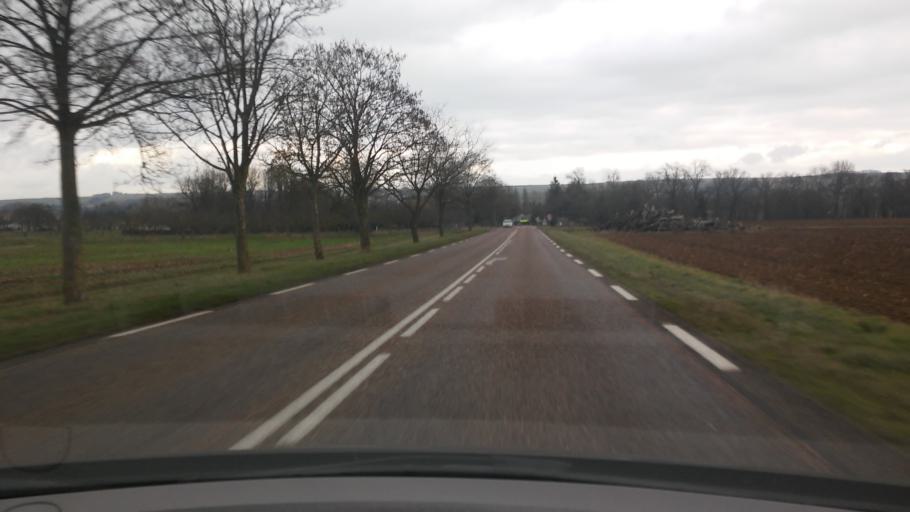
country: FR
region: Lorraine
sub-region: Departement de la Moselle
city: Courcelles-Chaussy
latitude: 49.1107
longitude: 6.3765
